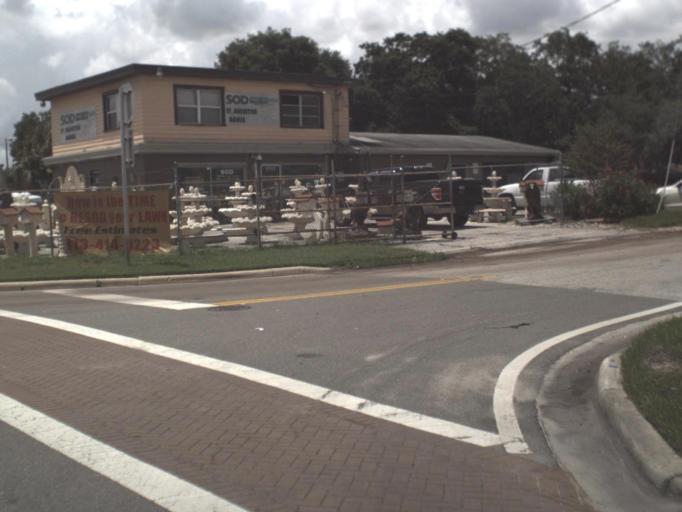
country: US
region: Florida
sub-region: Hillsborough County
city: University
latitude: 28.0329
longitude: -82.4490
